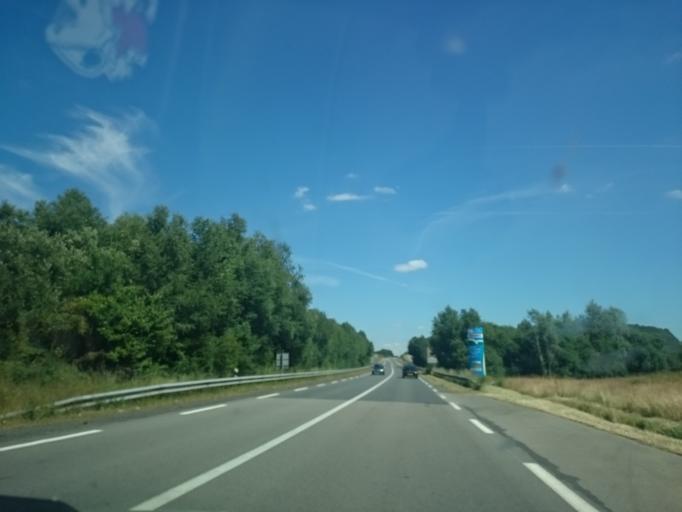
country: FR
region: Brittany
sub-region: Departement des Cotes-d'Armor
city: Plouguernevel
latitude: 48.2406
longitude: -3.2277
